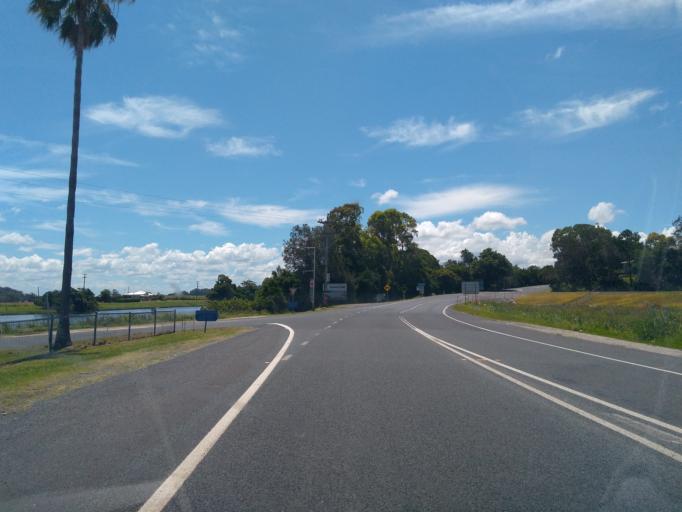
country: AU
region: New South Wales
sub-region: Clarence Valley
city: Maclean
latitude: -29.4720
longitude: 153.2050
